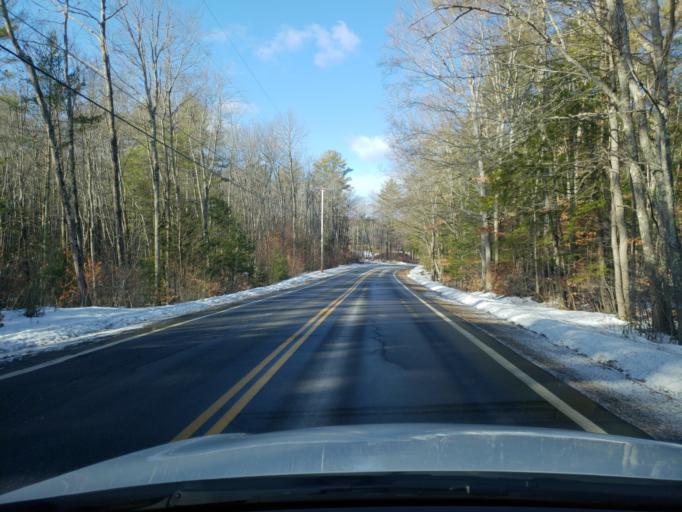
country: US
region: New Hampshire
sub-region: Hillsborough County
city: New Boston
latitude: 42.9854
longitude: -71.6981
